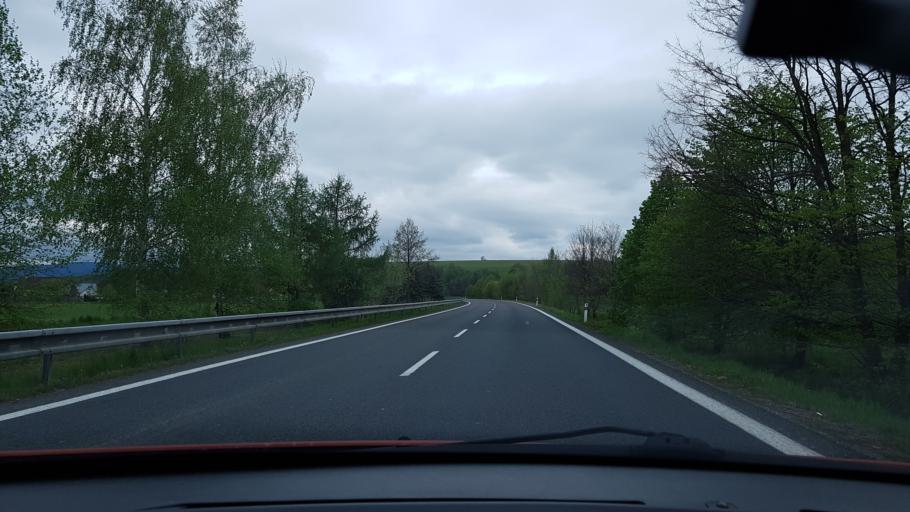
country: CZ
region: Olomoucky
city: Mikulovice
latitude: 50.3086
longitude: 17.3422
